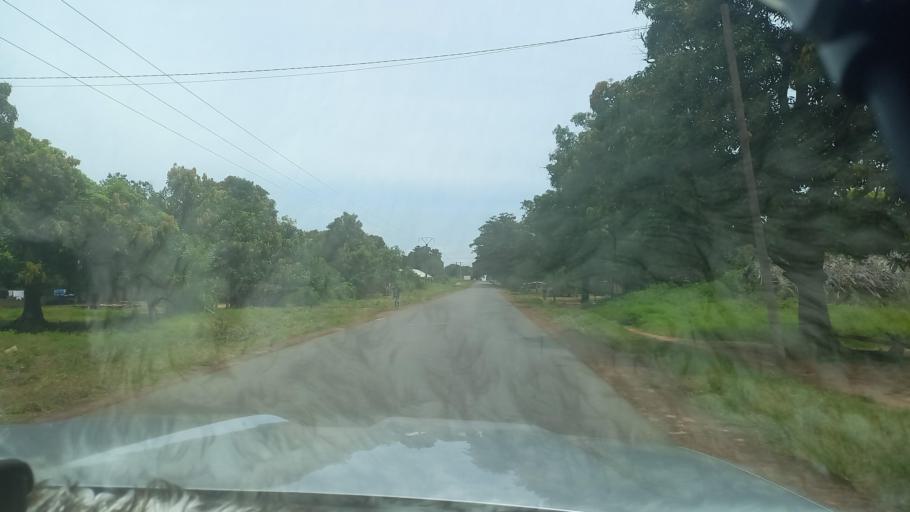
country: SN
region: Kolda
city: Marsassoum
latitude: 12.9601
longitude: -15.9944
